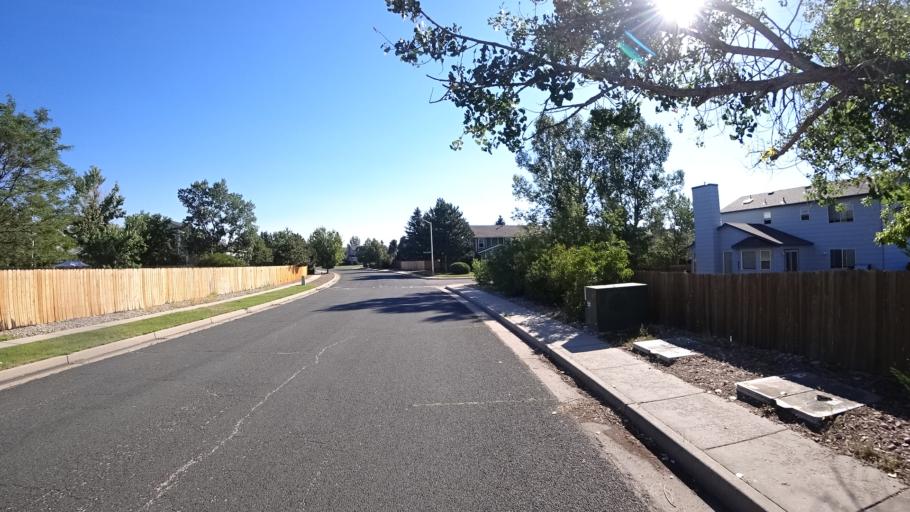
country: US
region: Colorado
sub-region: El Paso County
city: Black Forest
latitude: 38.9587
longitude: -104.7567
